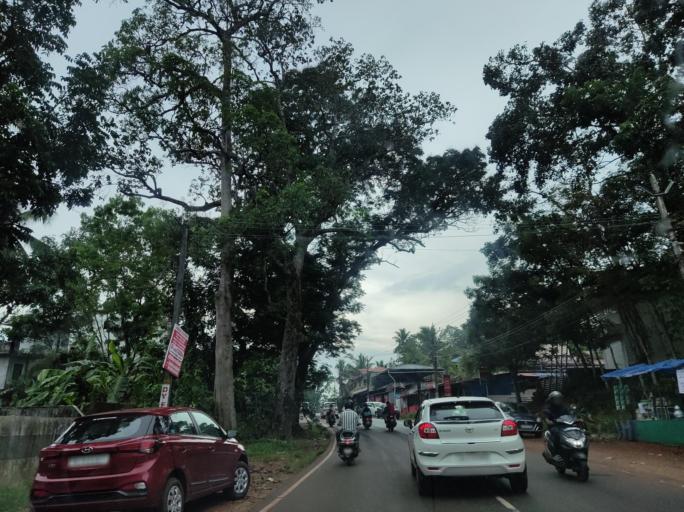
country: IN
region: Kerala
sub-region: Pattanamtitta
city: Adur
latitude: 9.1633
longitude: 76.7053
